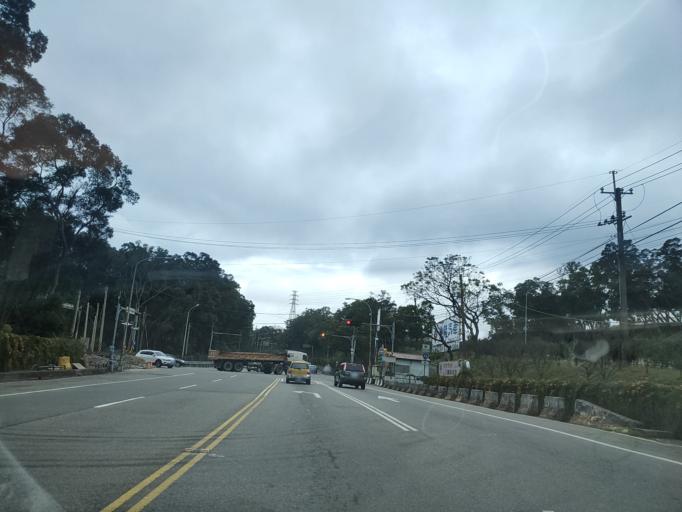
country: TW
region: Taiwan
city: Fengyuan
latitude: 24.3940
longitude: 120.7574
